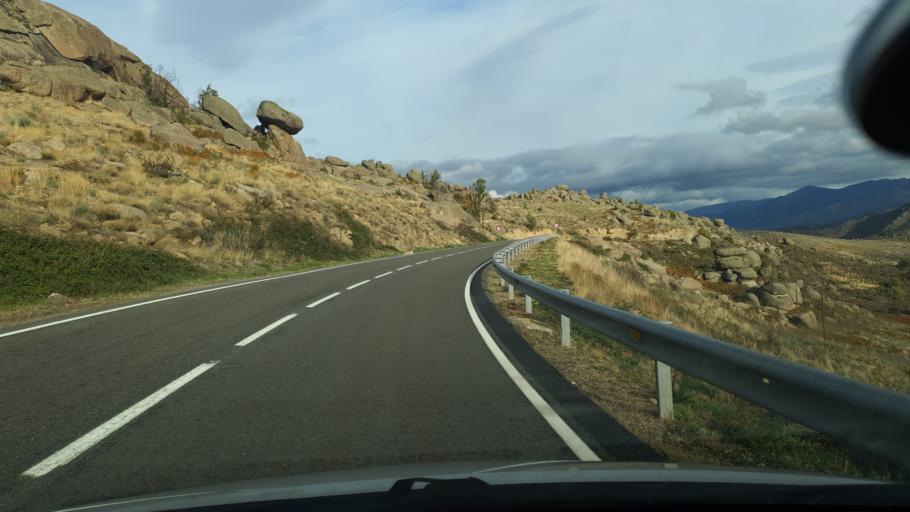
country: ES
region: Castille and Leon
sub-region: Provincia de Avila
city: Hoyocasero
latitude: 40.3929
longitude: -4.9518
